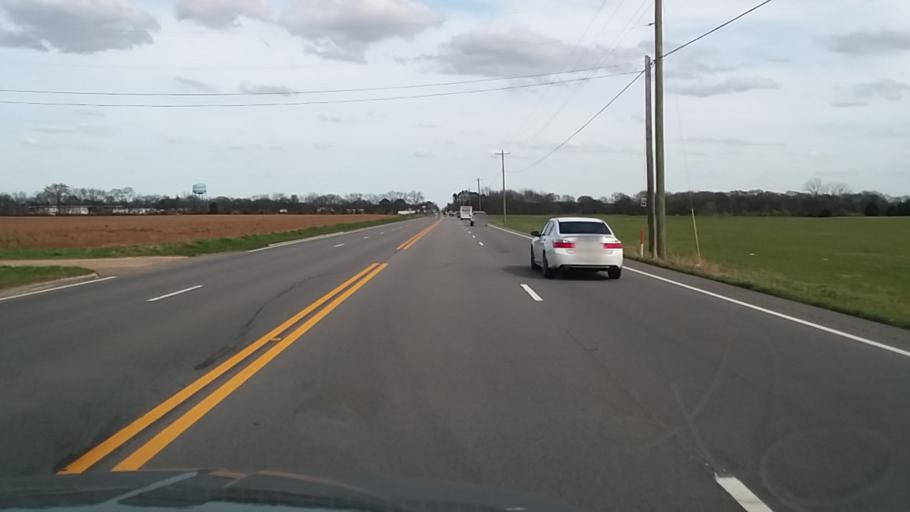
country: US
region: Alabama
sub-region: Lawrence County
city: Town Creek
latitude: 34.6817
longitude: -87.4294
